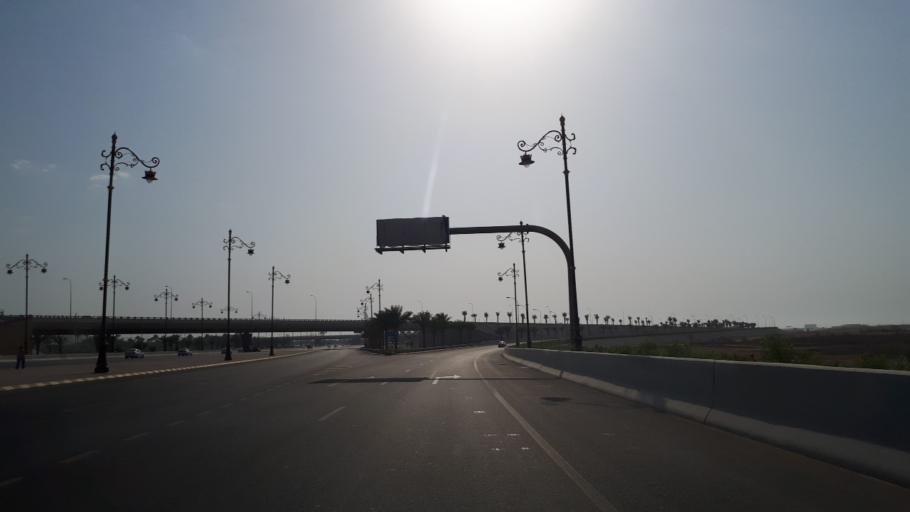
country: OM
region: Muhafazat Masqat
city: Bawshar
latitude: 23.5931
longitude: 58.3406
